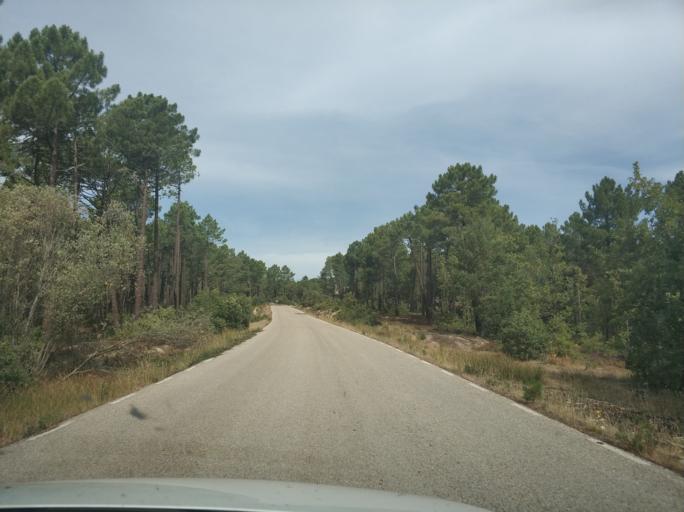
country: ES
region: Castille and Leon
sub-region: Provincia de Soria
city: Duruelo de la Sierra
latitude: 41.8887
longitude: -2.9404
